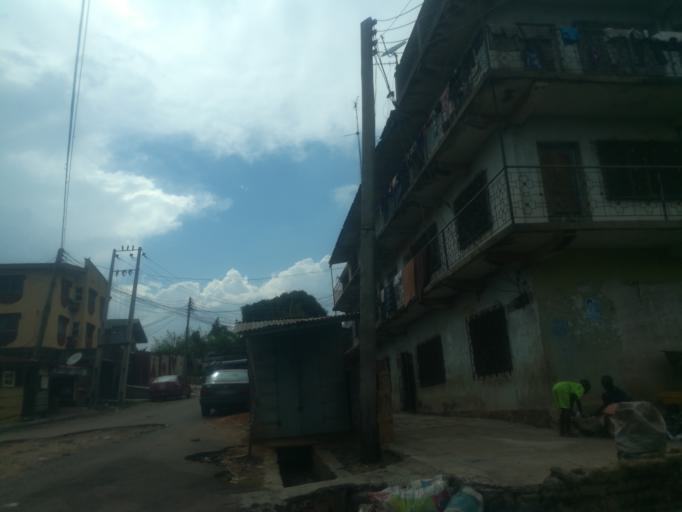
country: NG
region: Oyo
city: Ibadan
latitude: 7.4160
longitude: 3.8978
